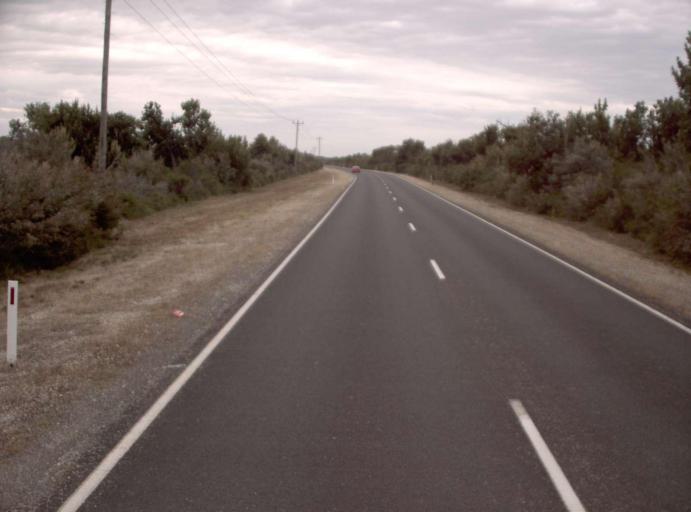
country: AU
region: Victoria
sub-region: Wellington
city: Sale
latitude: -38.1949
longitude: 147.3628
